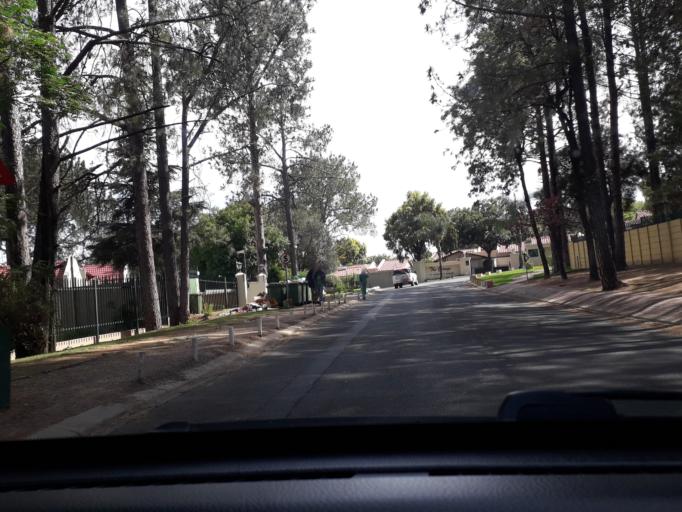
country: ZA
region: Gauteng
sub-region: City of Johannesburg Metropolitan Municipality
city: Diepsloot
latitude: -26.0377
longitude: 28.0313
